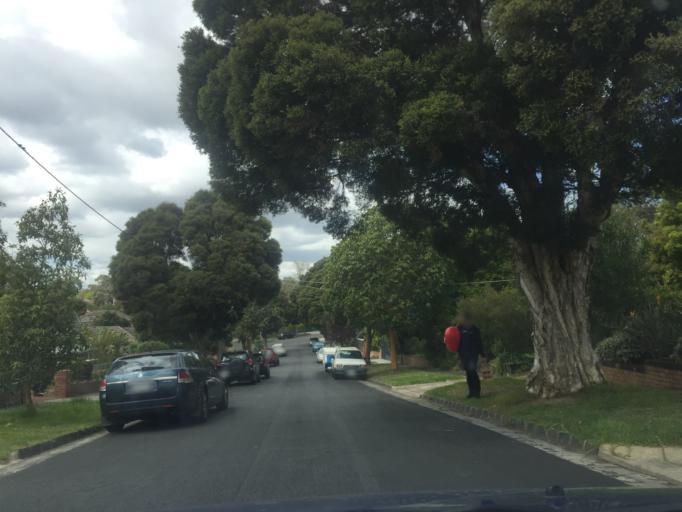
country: AU
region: Victoria
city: Alphington
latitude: -37.7946
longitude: 145.0387
